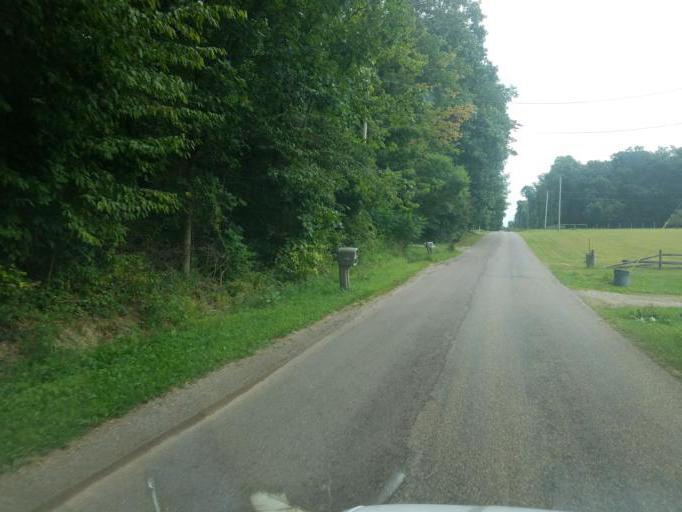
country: US
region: Ohio
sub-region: Sandusky County
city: Bellville
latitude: 40.5652
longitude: -82.3688
